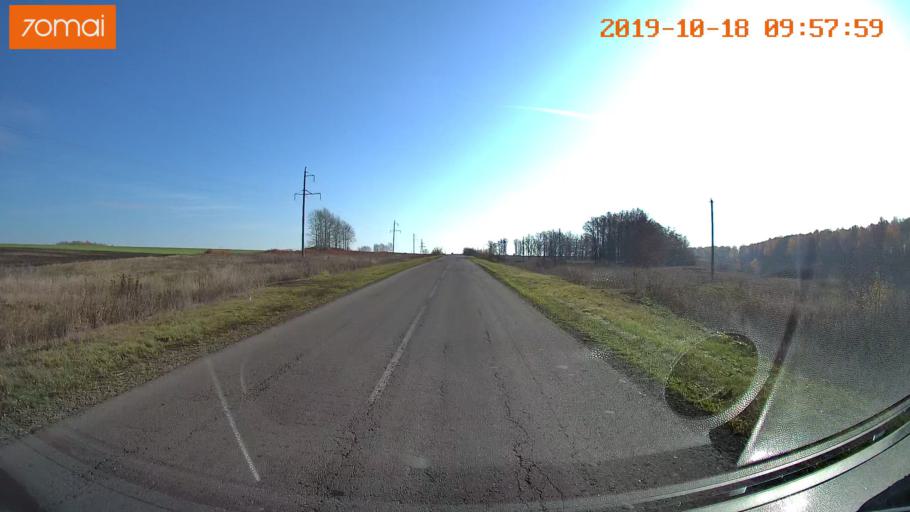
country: RU
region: Tula
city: Kurkino
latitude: 53.3760
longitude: 38.4289
